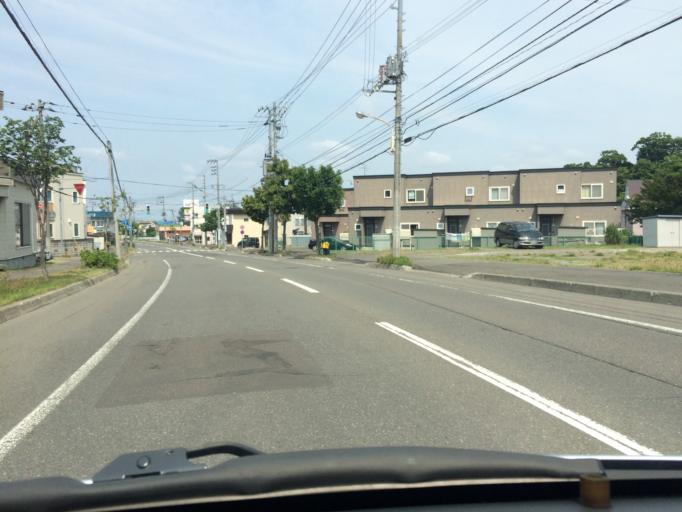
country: JP
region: Hokkaido
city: Sapporo
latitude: 43.0599
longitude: 141.2617
